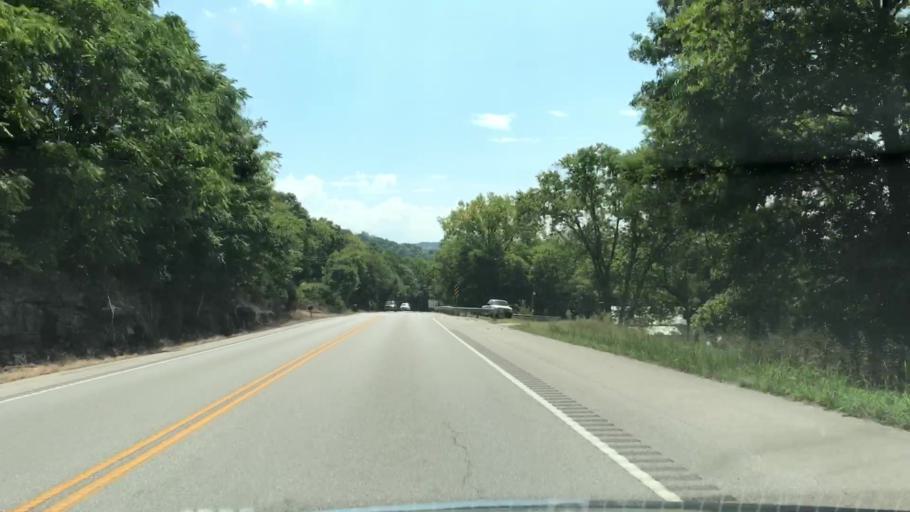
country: US
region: Tennessee
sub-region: Smith County
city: Carthage
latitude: 36.3213
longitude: -86.0156
